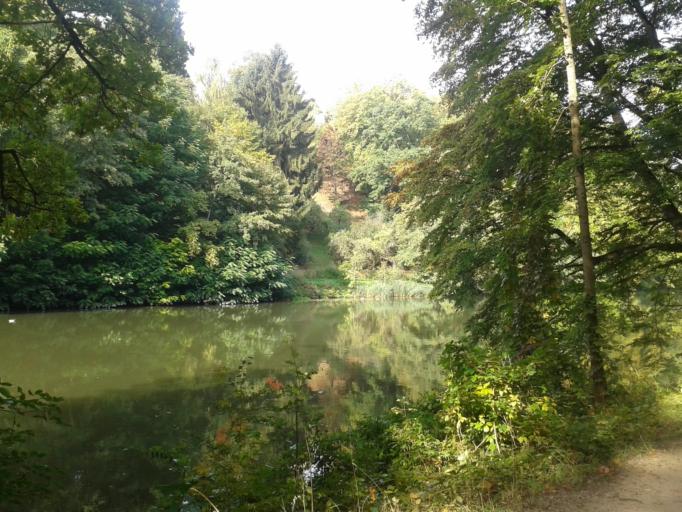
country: DE
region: Bavaria
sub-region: Upper Franconia
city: Bamberg
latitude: 49.8828
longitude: 10.8956
